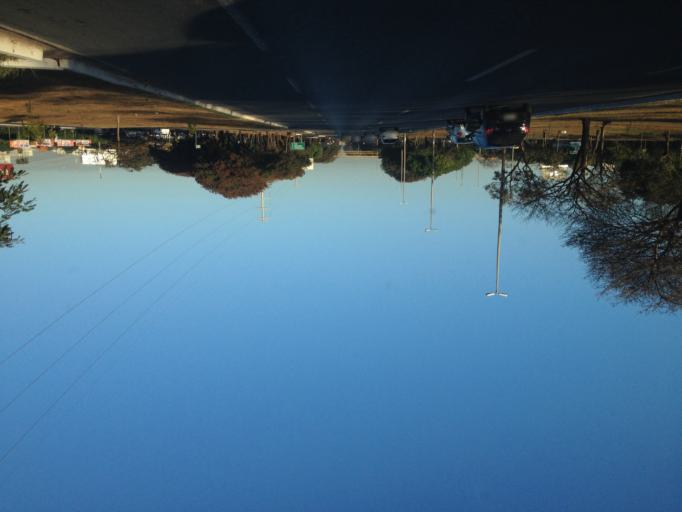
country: BR
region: Federal District
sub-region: Brasilia
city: Brasilia
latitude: -15.7931
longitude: -47.9441
